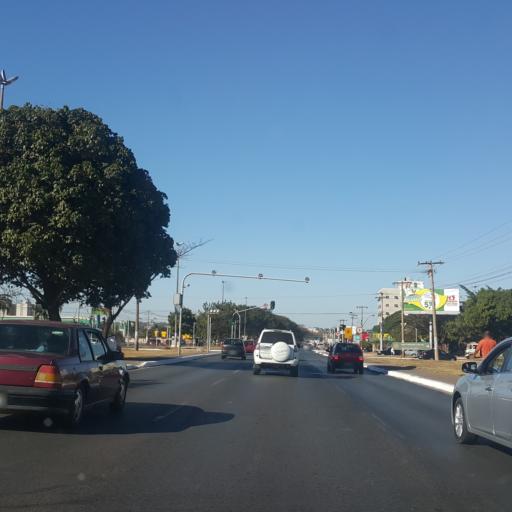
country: BR
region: Federal District
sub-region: Brasilia
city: Brasilia
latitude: -15.8107
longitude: -48.0910
